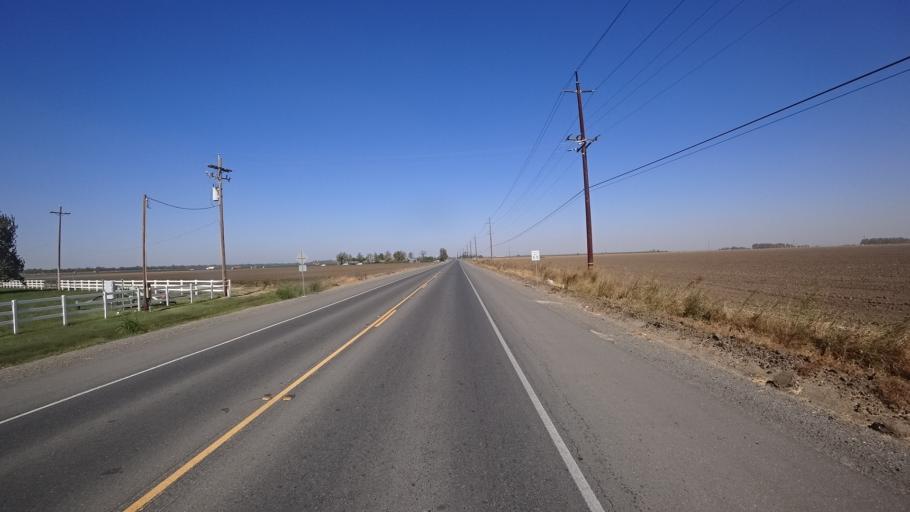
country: US
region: California
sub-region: Yolo County
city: Davis
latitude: 38.5944
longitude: -121.7302
